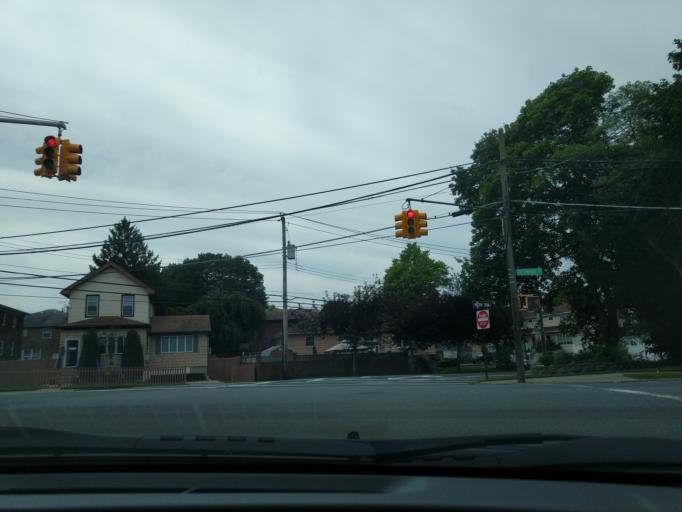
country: US
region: New York
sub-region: Richmond County
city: Staten Island
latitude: 40.5761
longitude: -74.1257
